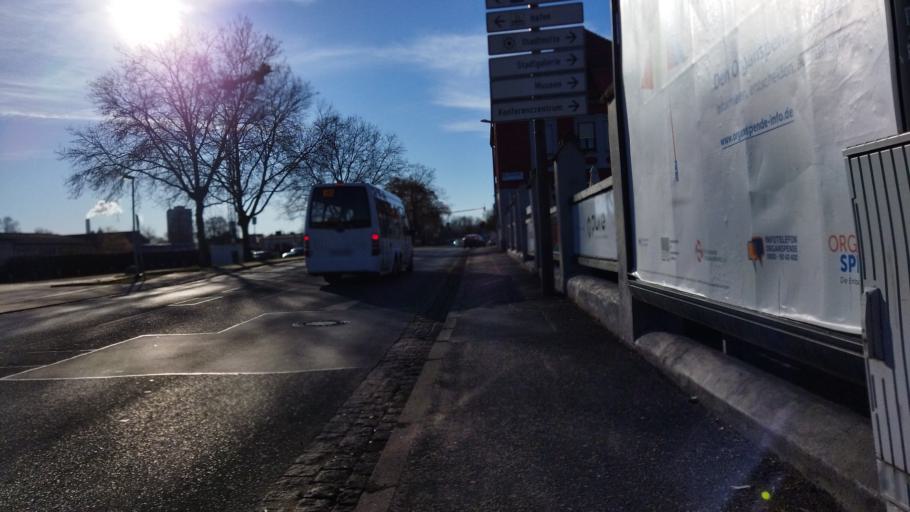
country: DE
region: Bavaria
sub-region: Regierungsbezirk Unterfranken
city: Sennfeld
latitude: 50.0391
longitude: 10.2416
